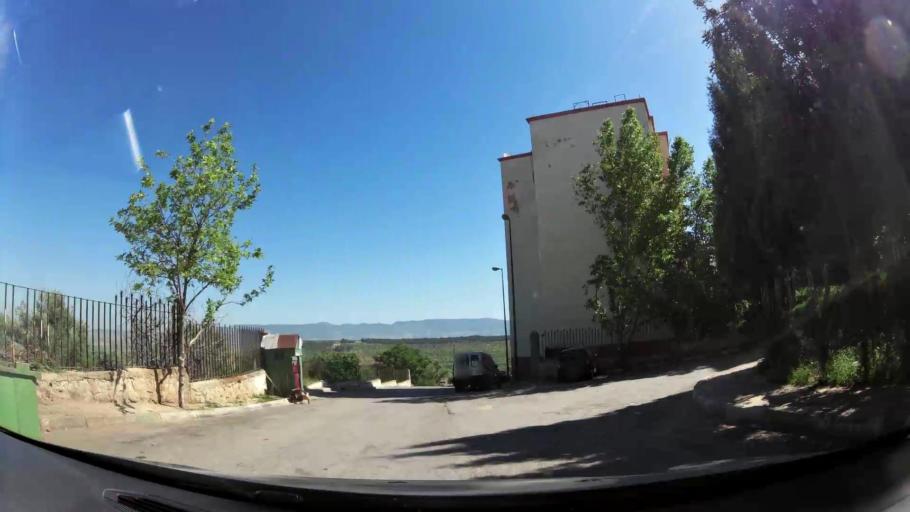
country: MA
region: Meknes-Tafilalet
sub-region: Meknes
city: Meknes
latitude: 33.9095
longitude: -5.5434
